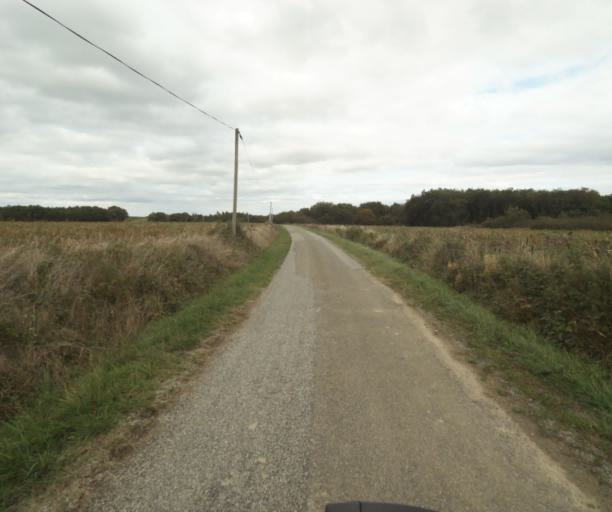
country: FR
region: Midi-Pyrenees
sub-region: Departement du Tarn-et-Garonne
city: Beaumont-de-Lomagne
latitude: 43.8407
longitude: 1.0935
